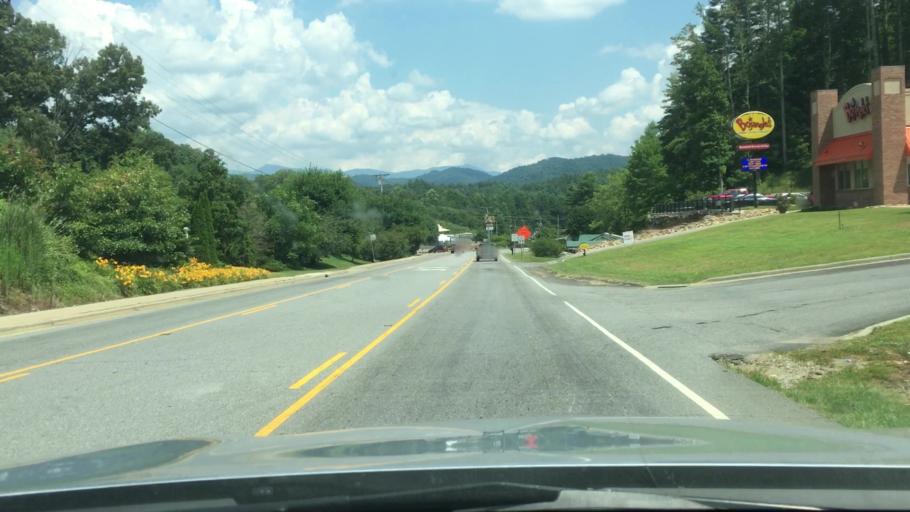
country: US
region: North Carolina
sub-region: Madison County
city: Mars Hill
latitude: 35.8225
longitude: -82.5432
